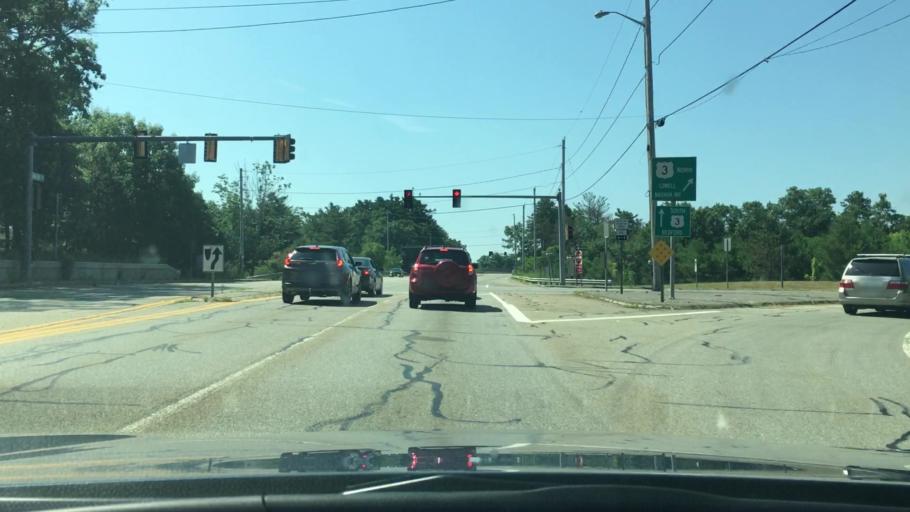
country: US
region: Massachusetts
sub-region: Middlesex County
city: Billerica
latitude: 42.5638
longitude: -71.2974
